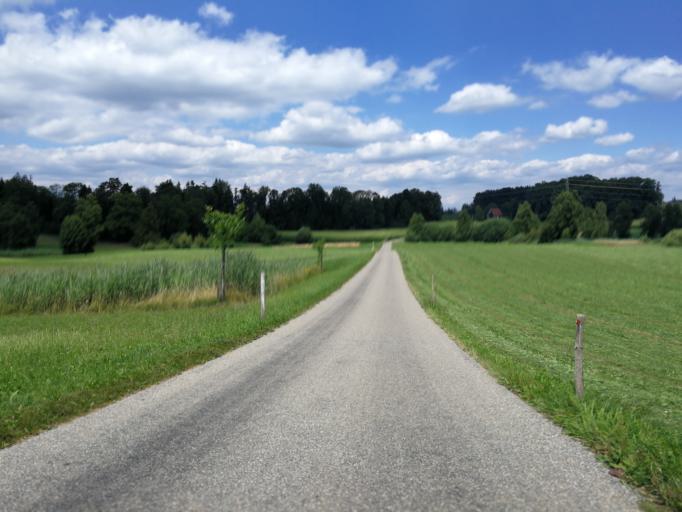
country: CH
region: Zurich
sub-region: Bezirk Hinwil
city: Wolfhausen
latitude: 47.2706
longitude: 8.7915
